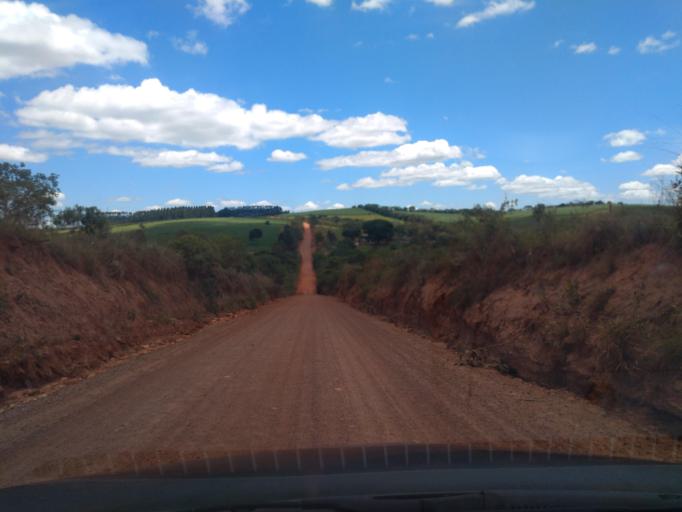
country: BR
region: Minas Gerais
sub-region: Lavras
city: Lavras
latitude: -21.5419
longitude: -44.9848
